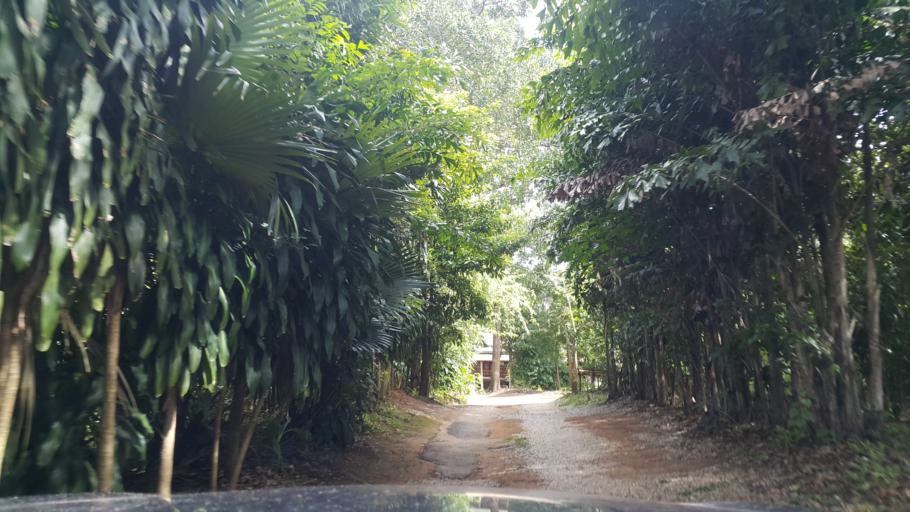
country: TH
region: Loei
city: Na Haeo
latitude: 17.5578
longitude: 100.9543
